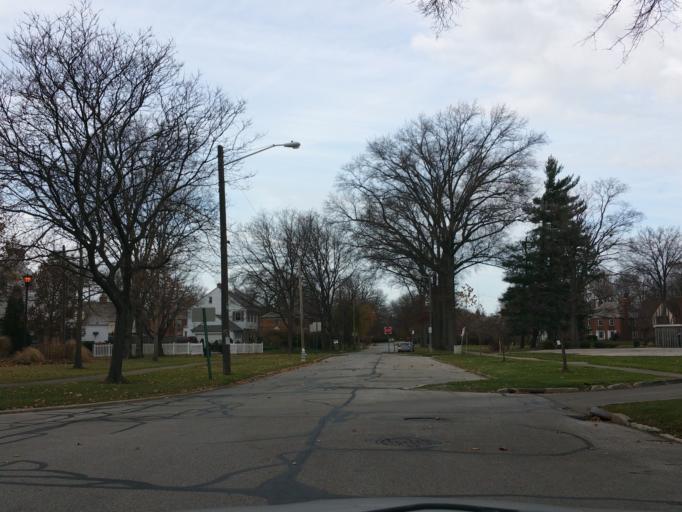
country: US
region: Ohio
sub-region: Cuyahoga County
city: Shaker Heights
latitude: 41.4621
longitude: -81.5401
